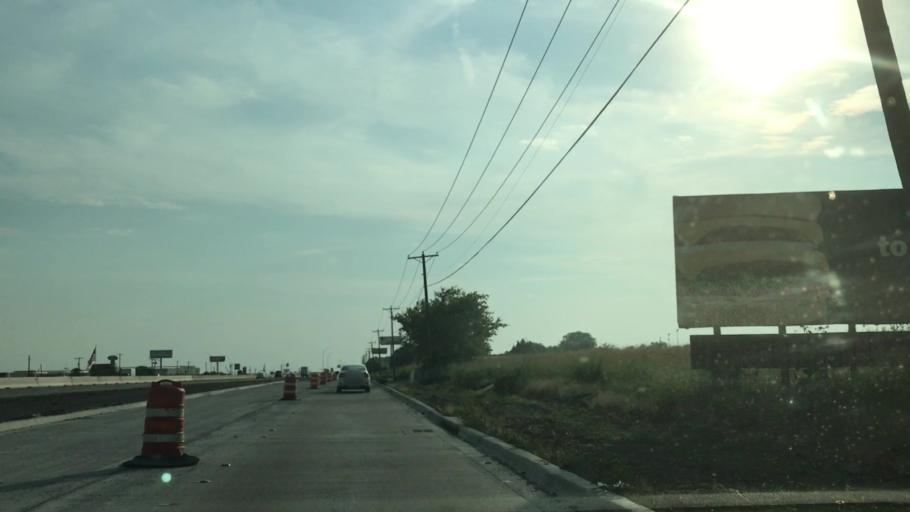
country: US
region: Texas
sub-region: Rockwall County
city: Rockwall
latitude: 32.9188
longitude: -96.4231
